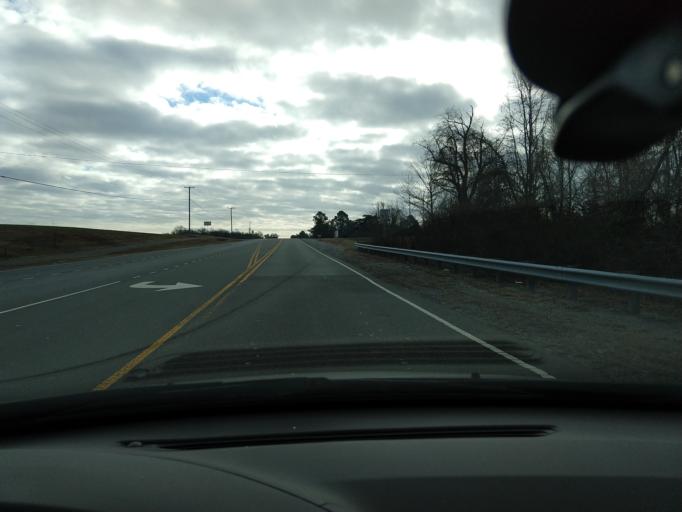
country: US
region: Virginia
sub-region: Henrico County
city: Montrose
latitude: 37.4651
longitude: -77.3825
